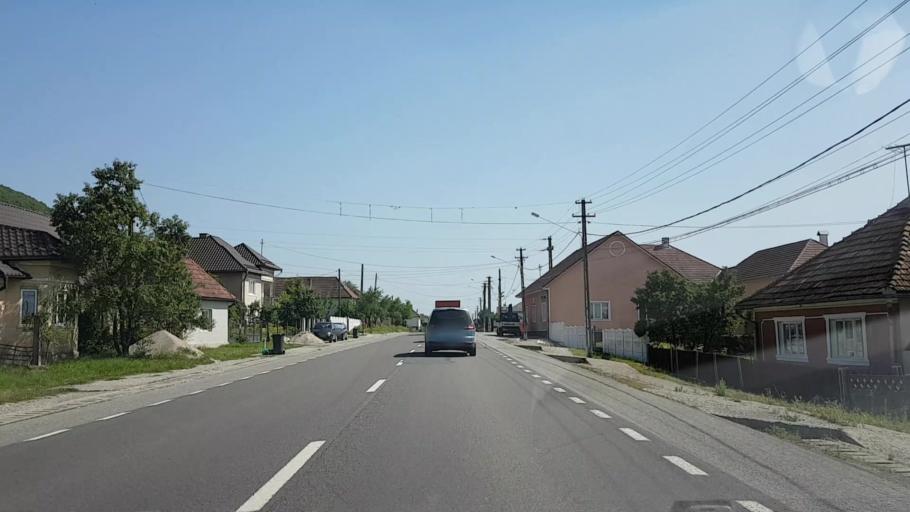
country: RO
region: Bistrita-Nasaud
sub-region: Comuna Sieu-Odorhei
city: Sieu-Odorhei
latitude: 47.1452
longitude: 24.3064
